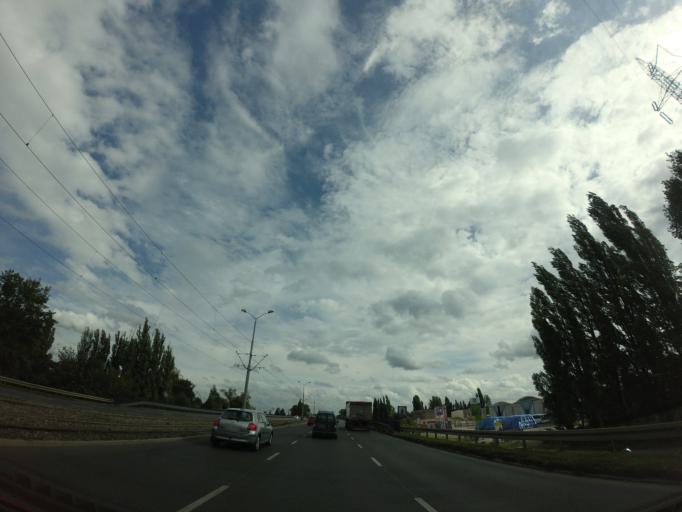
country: PL
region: West Pomeranian Voivodeship
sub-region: Szczecin
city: Szczecin
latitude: 53.4095
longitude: 14.5842
